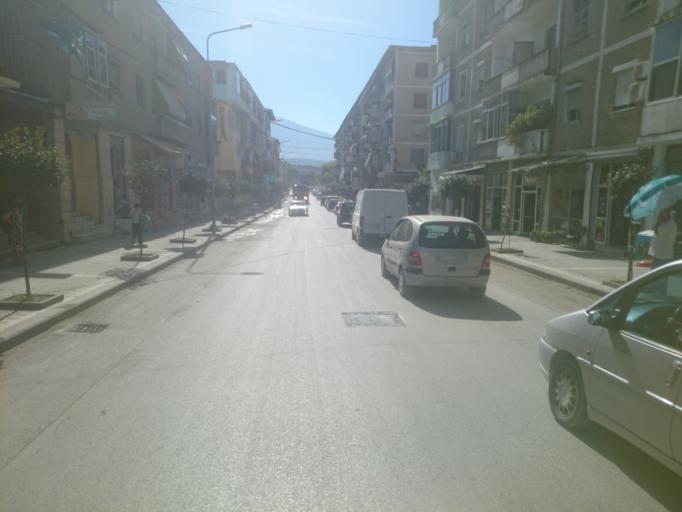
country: AL
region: Berat
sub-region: Rrethi i Beratit
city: Berat
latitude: 40.7049
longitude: 19.9528
